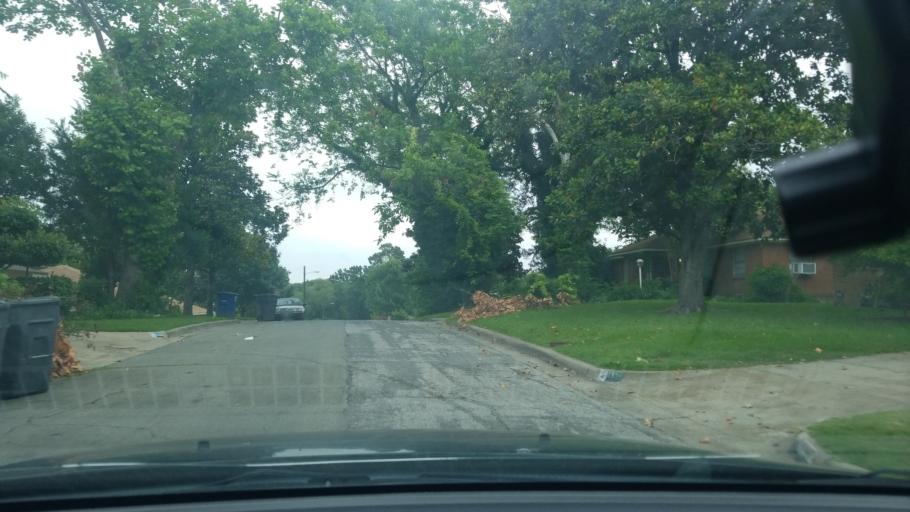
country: US
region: Texas
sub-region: Dallas County
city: Balch Springs
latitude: 32.7603
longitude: -96.6904
